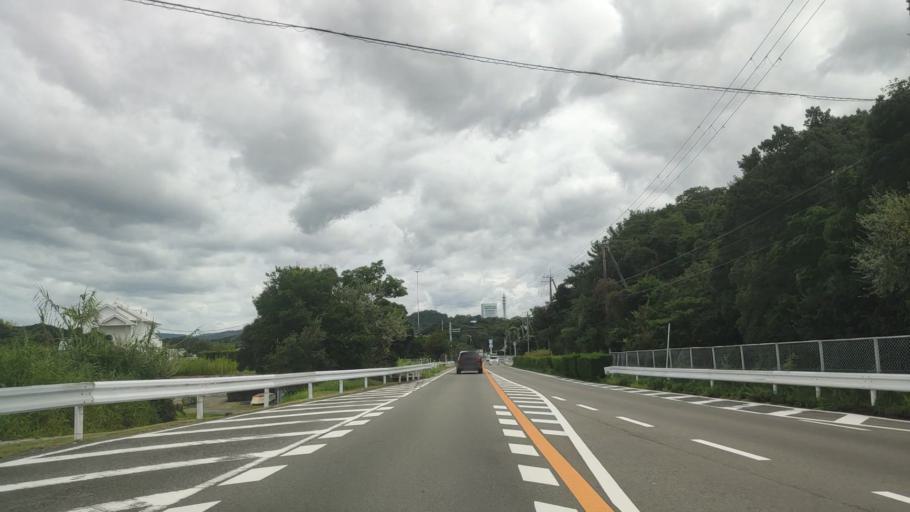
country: JP
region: Wakayama
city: Tanabe
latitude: 33.7016
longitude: 135.3910
